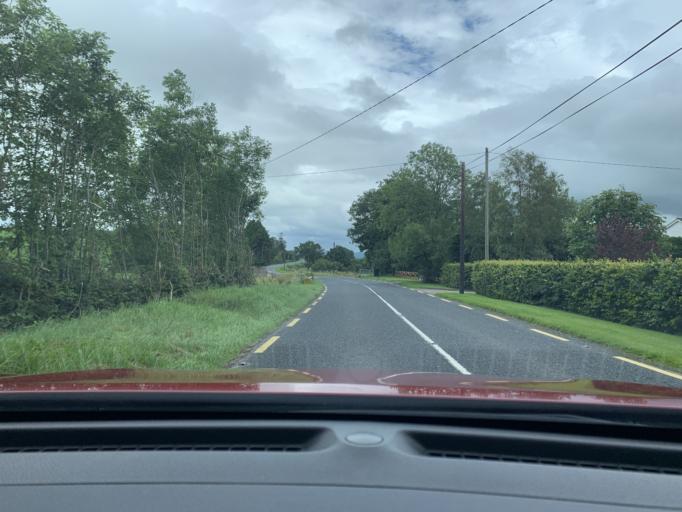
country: IE
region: Ulster
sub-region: County Donegal
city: Convoy
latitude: 54.7975
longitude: -7.6715
